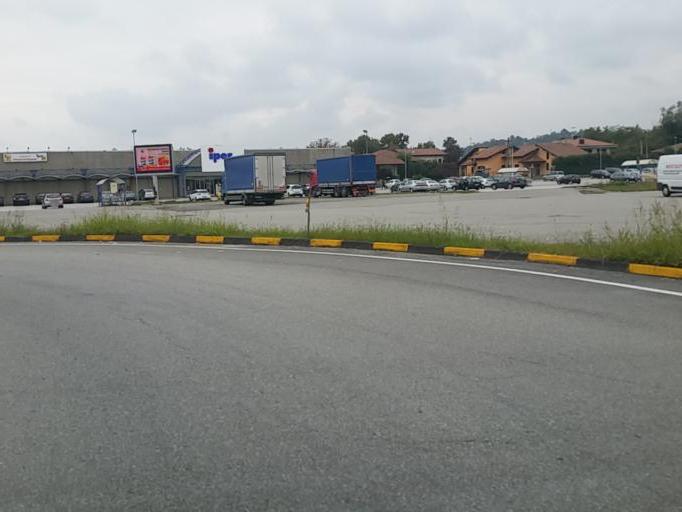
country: IT
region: Piedmont
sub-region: Provincia di Novara
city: Gozzano
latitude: 45.7356
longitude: 8.4400
